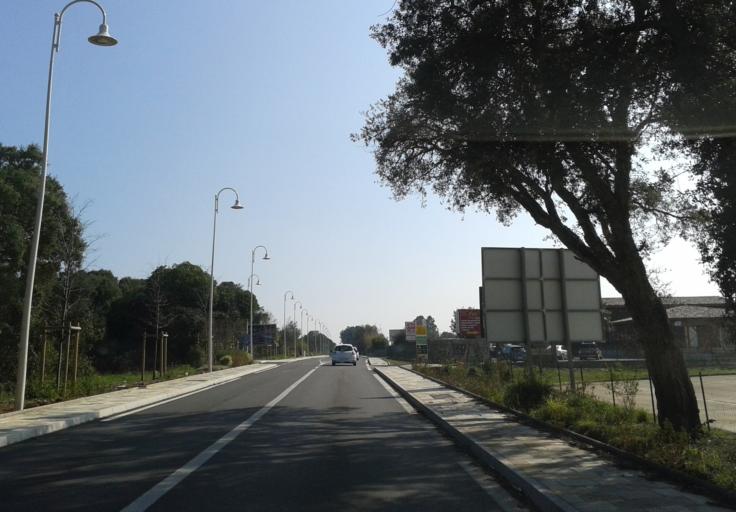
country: FR
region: Corsica
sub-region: Departement de la Haute-Corse
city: San-Nicolao
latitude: 42.3541
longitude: 9.5316
